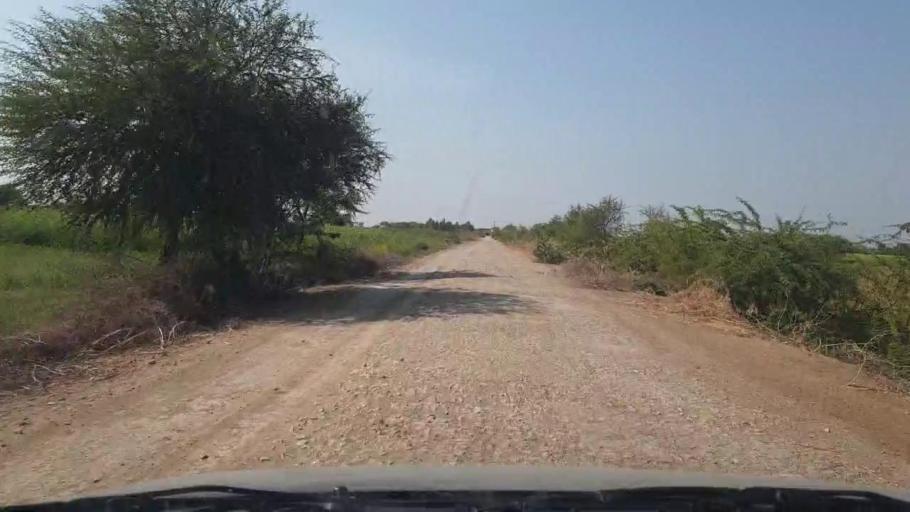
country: PK
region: Sindh
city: Samaro
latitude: 25.1893
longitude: 69.3558
